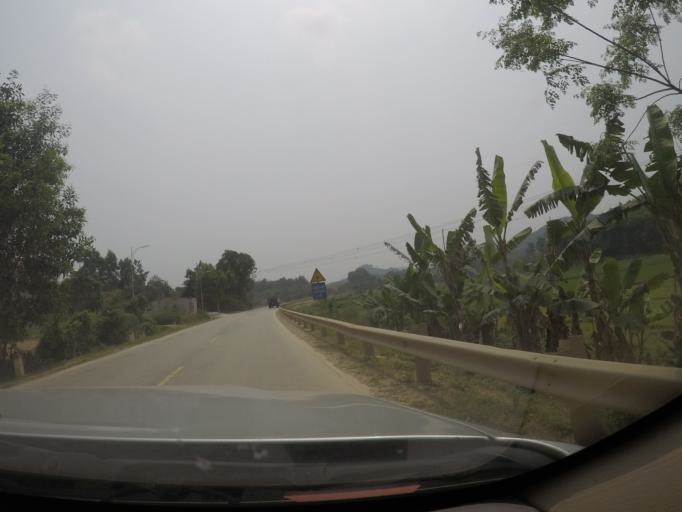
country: VN
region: Thanh Hoa
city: Thi Tran Yen Cat
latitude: 19.7342
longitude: 105.4270
